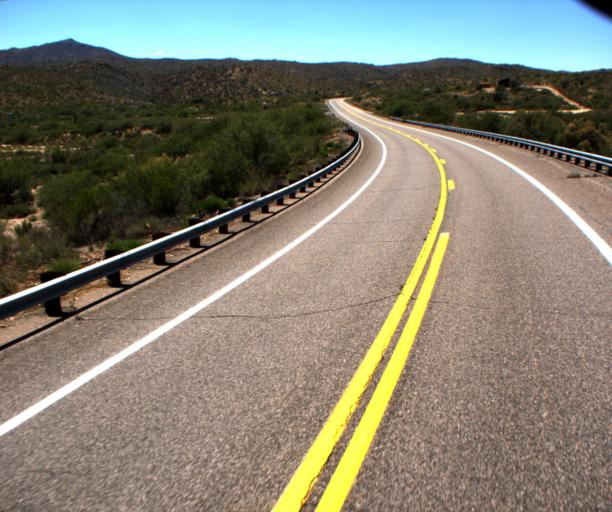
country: US
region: Arizona
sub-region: Yavapai County
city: Bagdad
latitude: 34.5173
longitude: -113.0775
